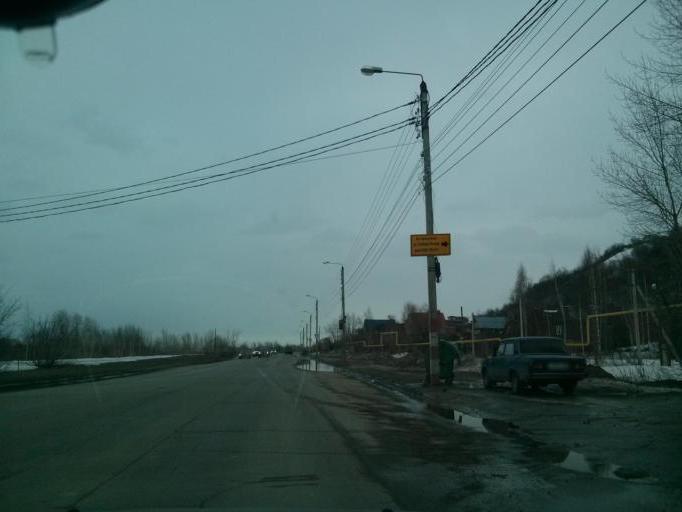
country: RU
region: Nizjnij Novgorod
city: Bor
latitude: 56.3124
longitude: 44.0882
